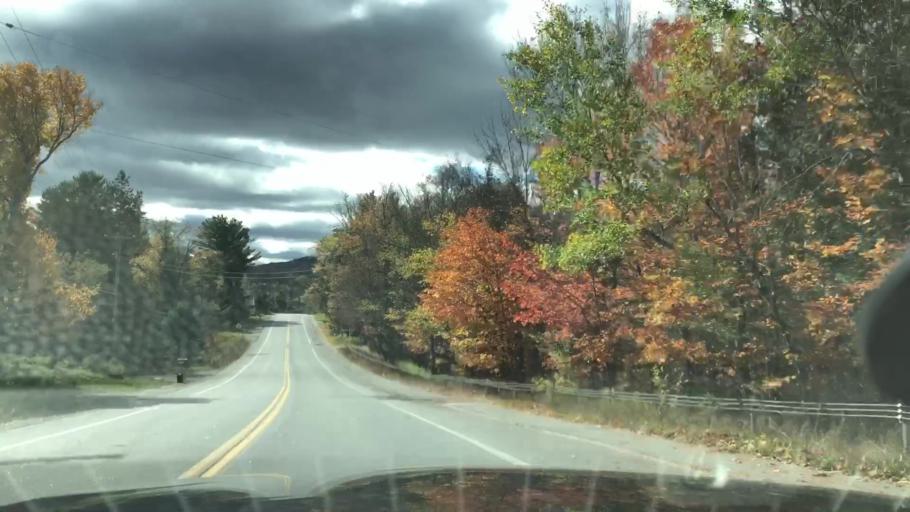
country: US
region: New York
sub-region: Essex County
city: Lake Placid
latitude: 43.9714
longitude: -74.1550
